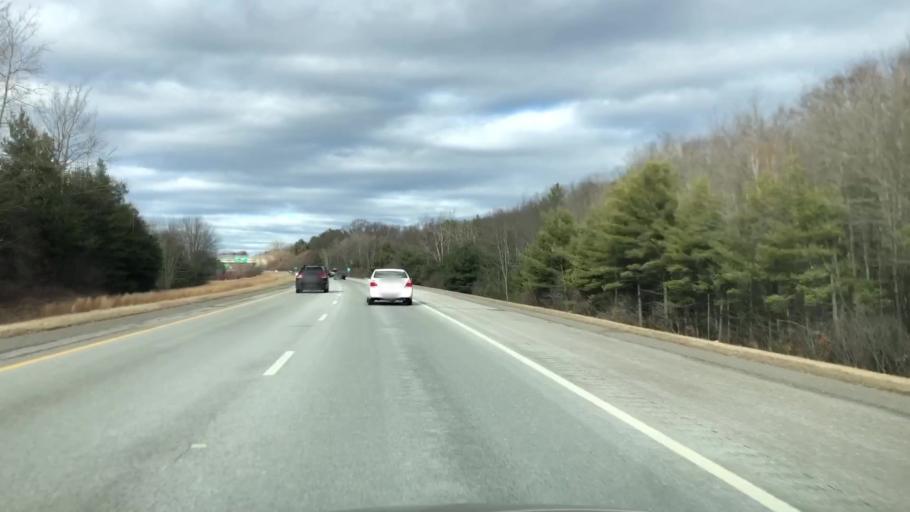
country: US
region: Massachusetts
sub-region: Worcester County
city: Leominster
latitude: 42.5027
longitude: -71.7205
